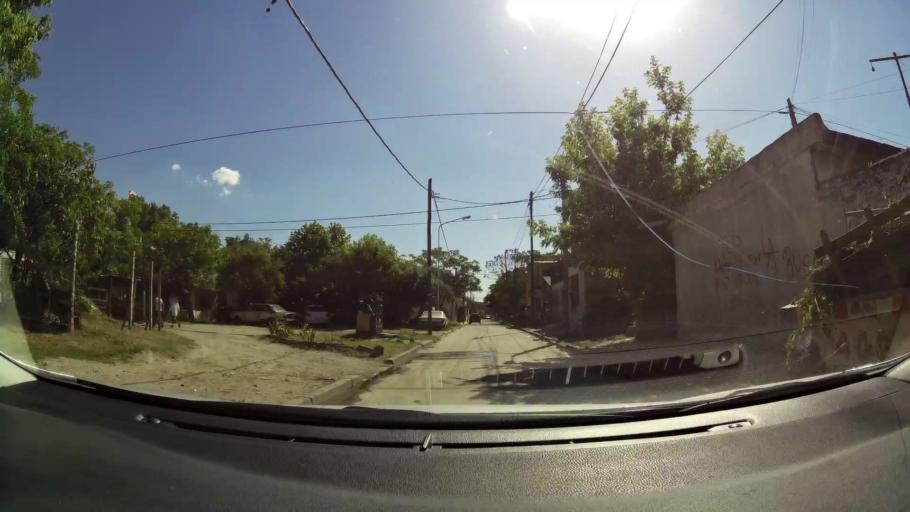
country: AR
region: Buenos Aires F.D.
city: Villa Lugano
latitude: -34.7090
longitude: -58.4789
